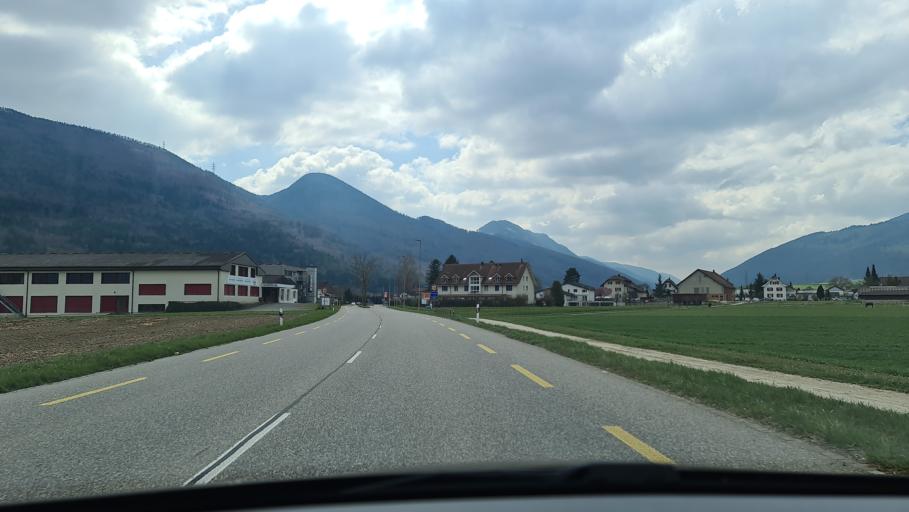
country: CH
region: Solothurn
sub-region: Bezirk Thal
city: Matzendorf
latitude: 47.3057
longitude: 7.6356
